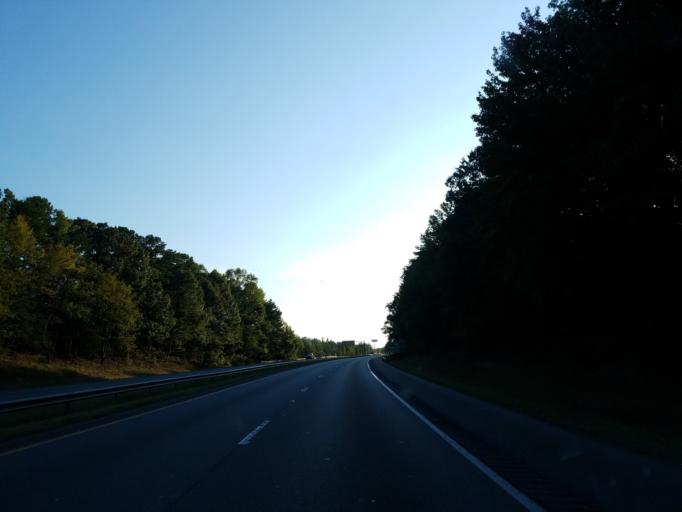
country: US
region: North Carolina
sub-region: Cleveland County
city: Kings Mountain
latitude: 35.2353
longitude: -81.3163
